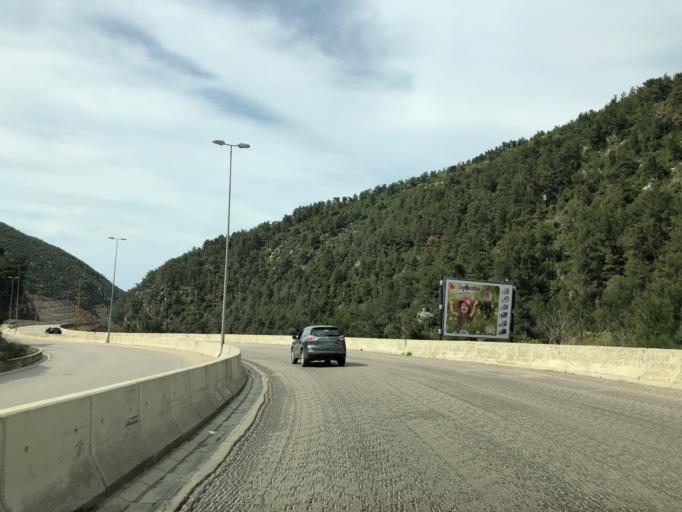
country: LB
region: Mont-Liban
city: Bhamdoun el Mhatta
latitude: 33.8944
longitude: 35.6572
